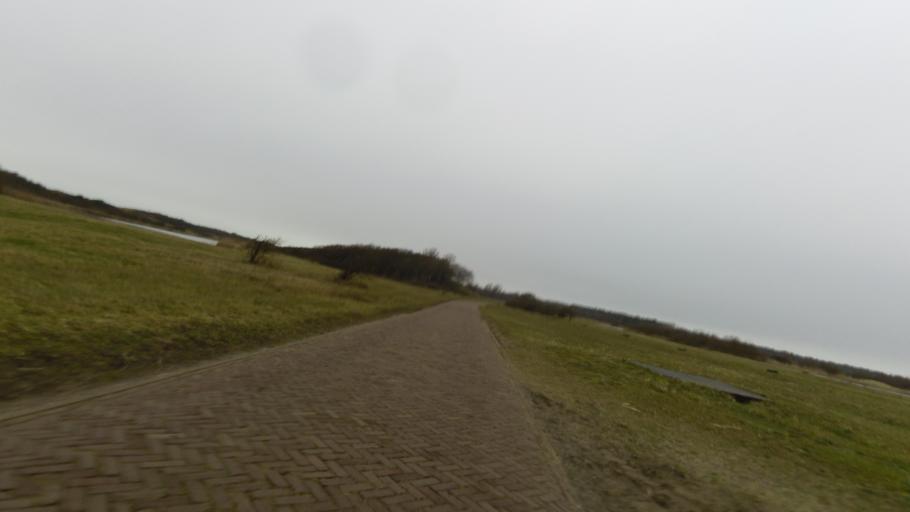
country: NL
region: North Holland
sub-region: Gemeente Castricum
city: Castricum
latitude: 52.5486
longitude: 4.6186
